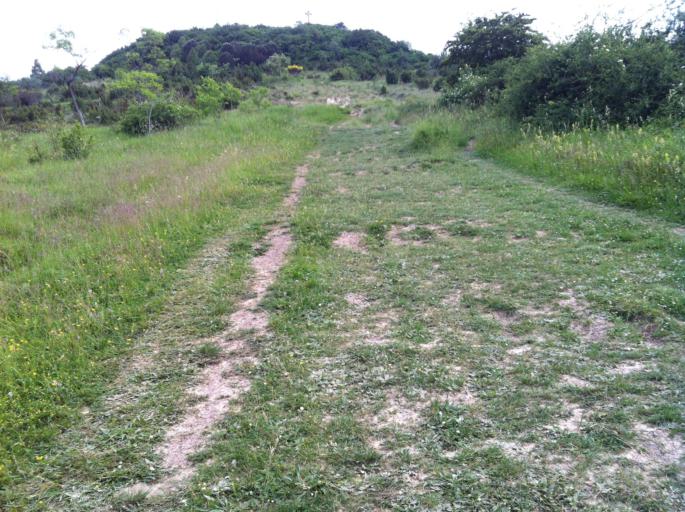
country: ES
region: Basque Country
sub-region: Provincia de Alava
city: Gasteiz / Vitoria
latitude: 42.8193
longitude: -2.6621
